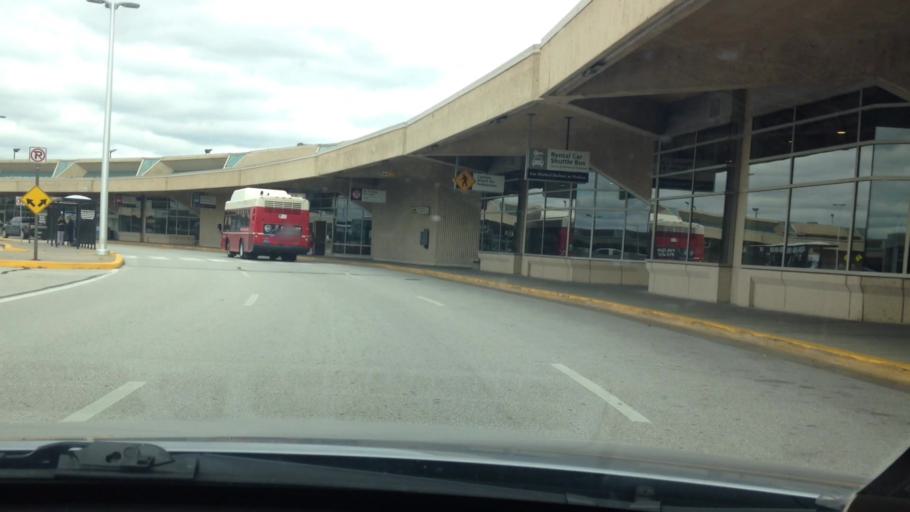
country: US
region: Missouri
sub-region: Platte County
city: Weatherby Lake
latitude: 39.2936
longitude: -94.7123
